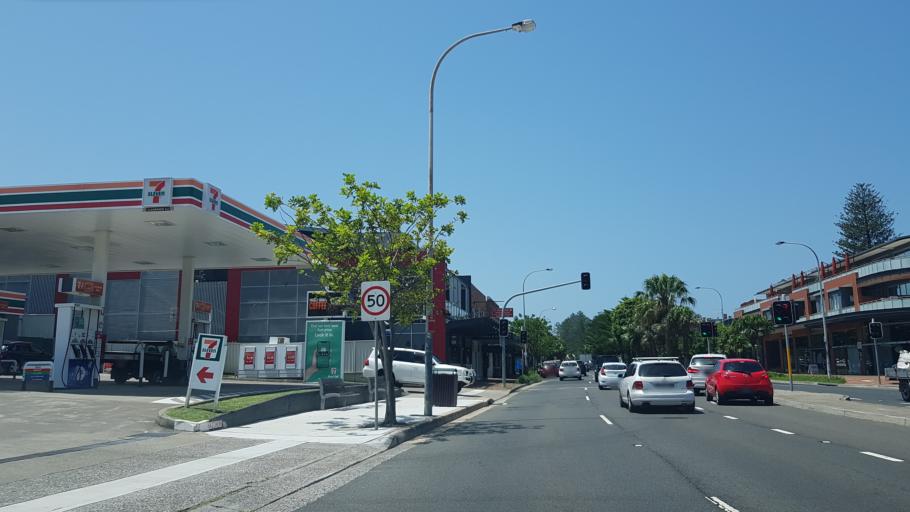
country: AU
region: New South Wales
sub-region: Pittwater
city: Newport
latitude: -33.6567
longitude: 151.3182
